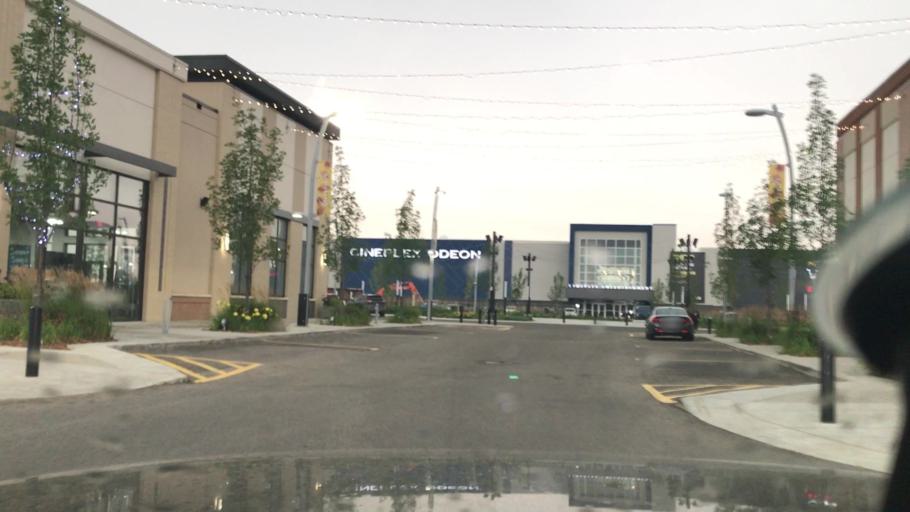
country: CA
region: Alberta
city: Devon
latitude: 53.4350
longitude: -113.6036
